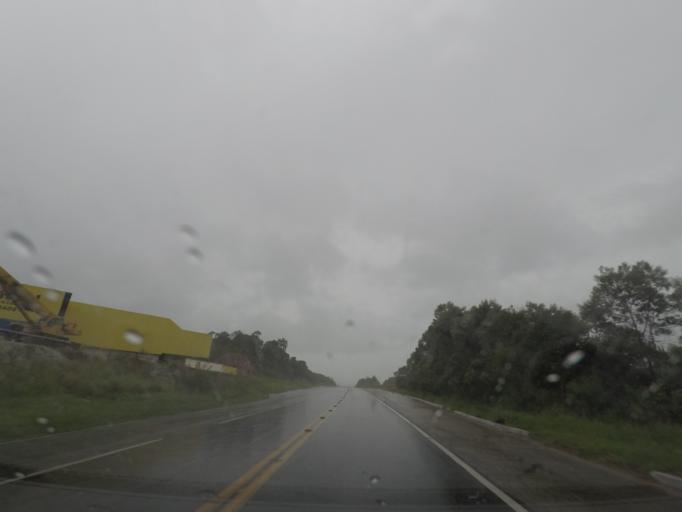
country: BR
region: Parana
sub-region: Almirante Tamandare
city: Almirante Tamandare
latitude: -25.3625
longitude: -49.3163
